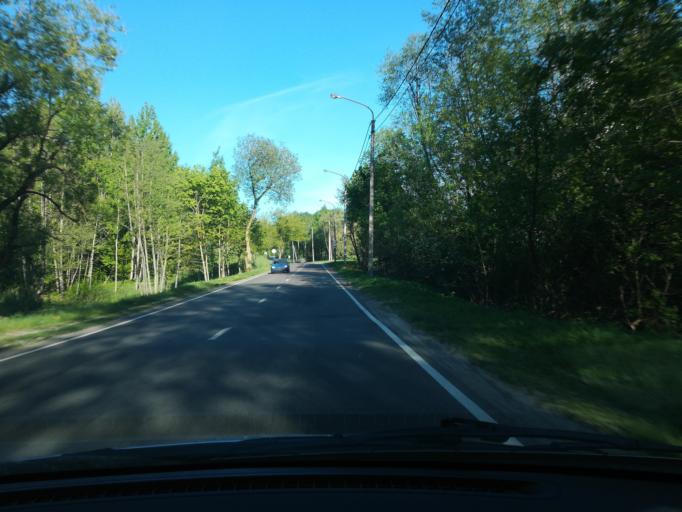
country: LT
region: Vilnius County
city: Rasos
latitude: 54.6668
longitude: 25.3225
